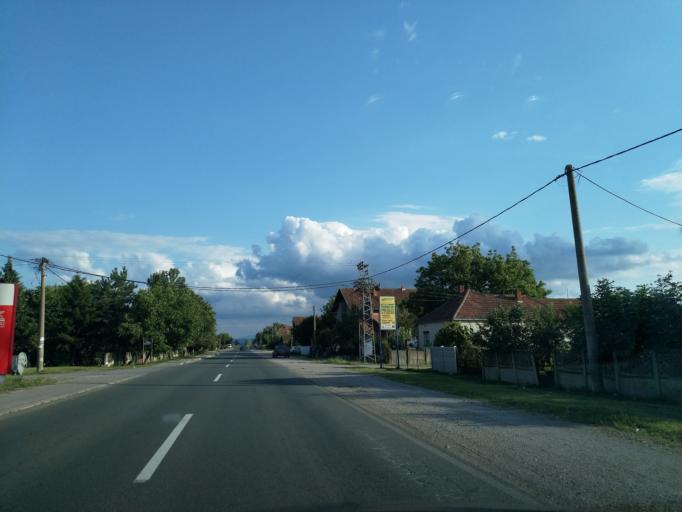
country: RS
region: Central Serbia
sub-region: Pomoravski Okrug
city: Paracin
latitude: 43.8051
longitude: 21.4213
